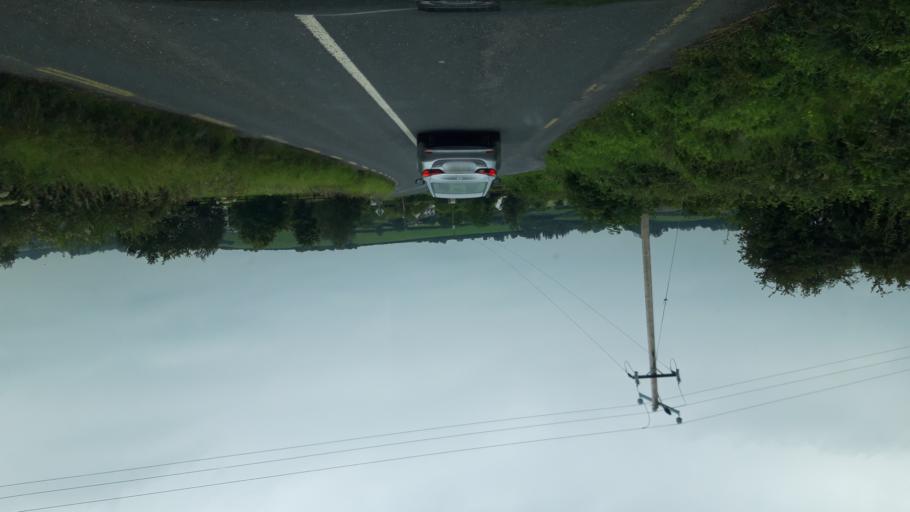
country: IE
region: Munster
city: Fethard
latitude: 52.4607
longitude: -7.7030
